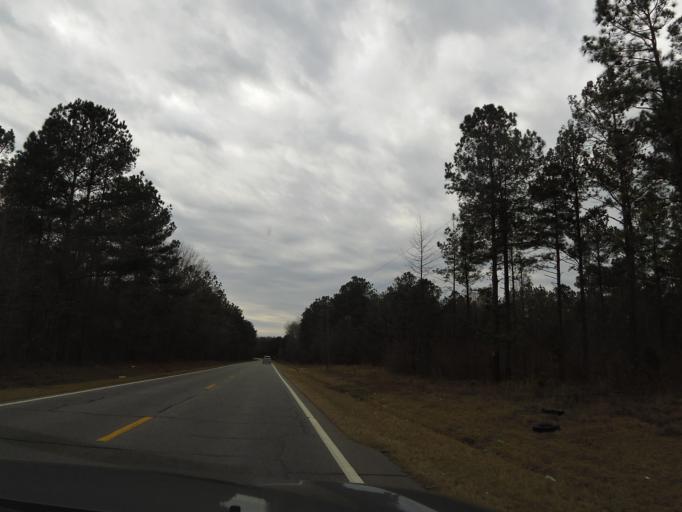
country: US
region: North Carolina
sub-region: Edgecombe County
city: Tarboro
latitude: 36.0091
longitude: -77.5313
